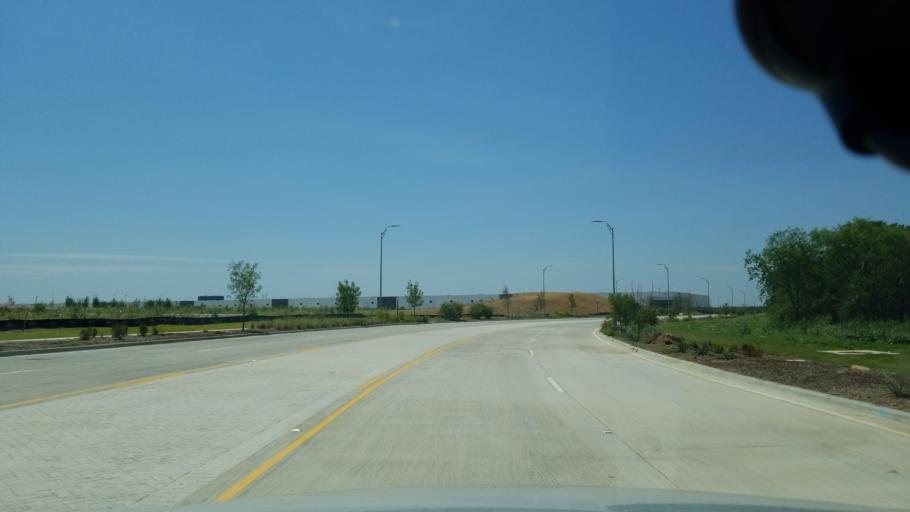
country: US
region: Texas
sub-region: Tarrant County
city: Euless
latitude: 32.8491
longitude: -97.0312
